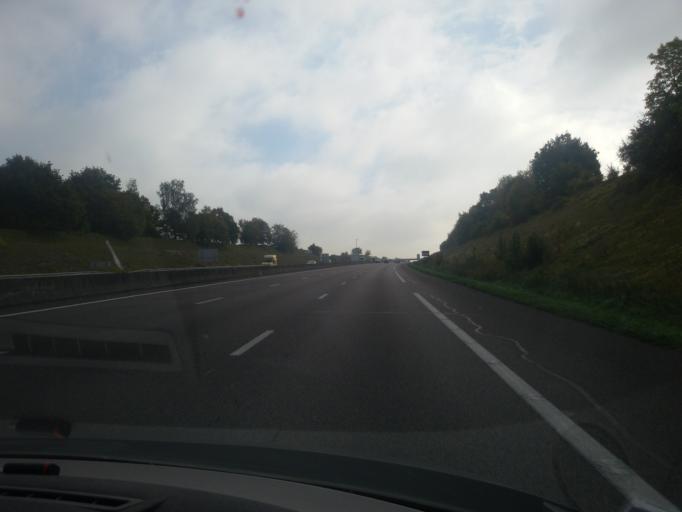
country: FR
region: Haute-Normandie
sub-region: Departement de l'Eure
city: Saint-Pierre-du-Vauvray
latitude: 49.2327
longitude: 1.2040
